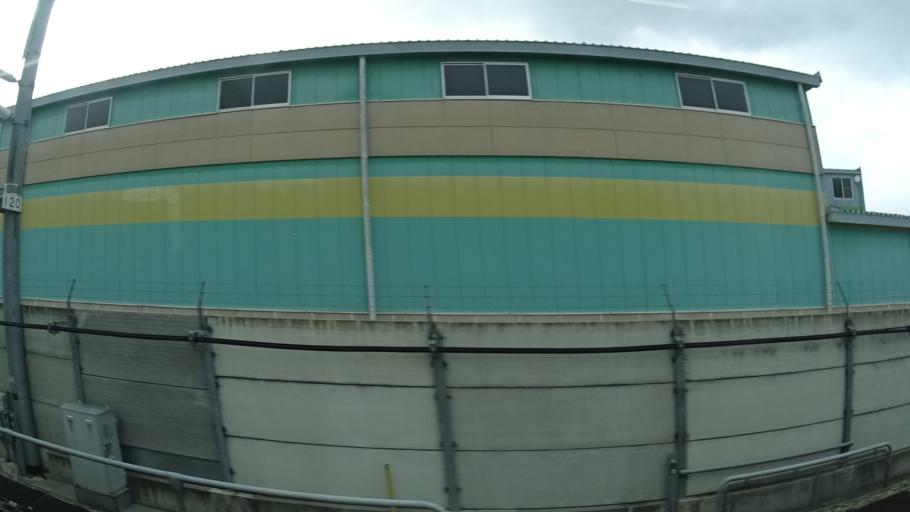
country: JP
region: Nagano
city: Nagano-shi
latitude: 36.6583
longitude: 138.2111
